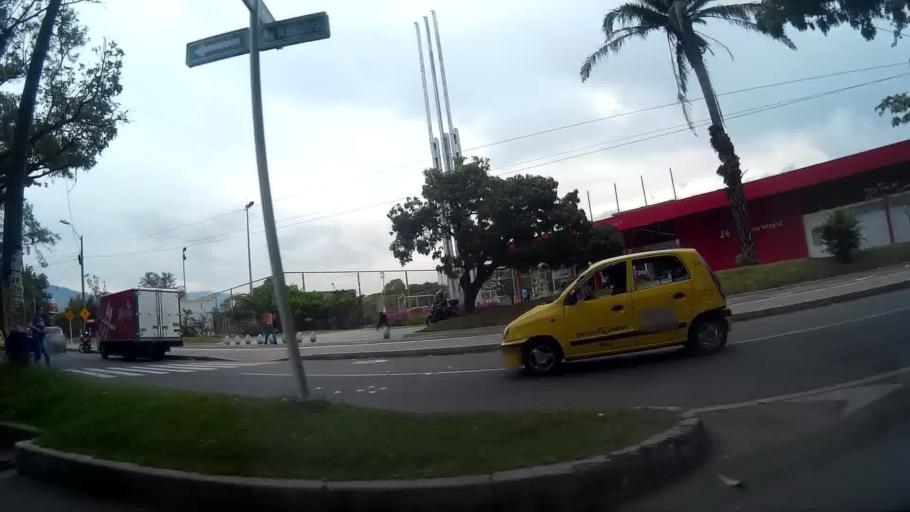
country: CO
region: Antioquia
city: Medellin
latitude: 6.2412
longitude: -75.5916
